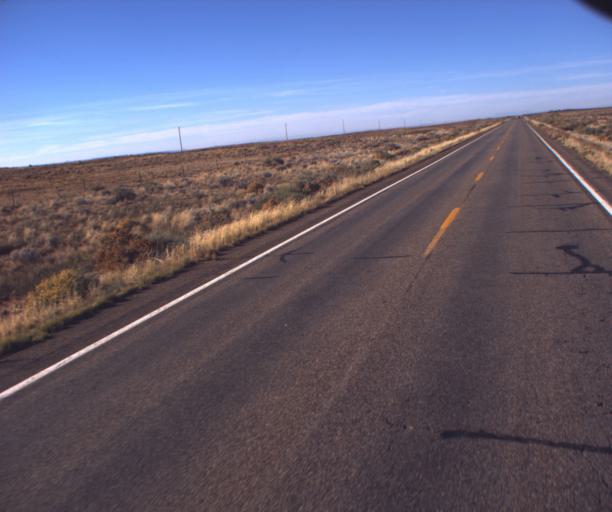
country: US
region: Arizona
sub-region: Coconino County
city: Kaibito
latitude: 36.7002
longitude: -111.2650
